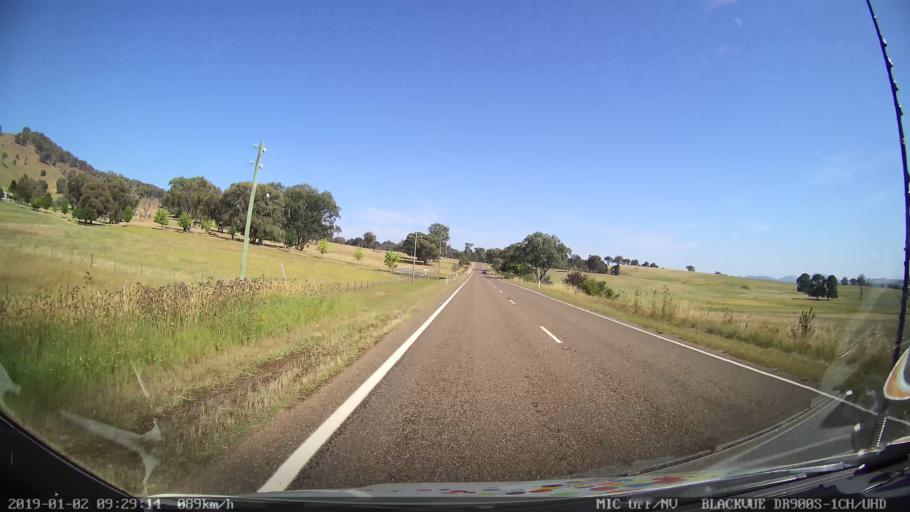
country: AU
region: New South Wales
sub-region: Tumut Shire
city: Tumut
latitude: -35.3407
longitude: 148.2443
